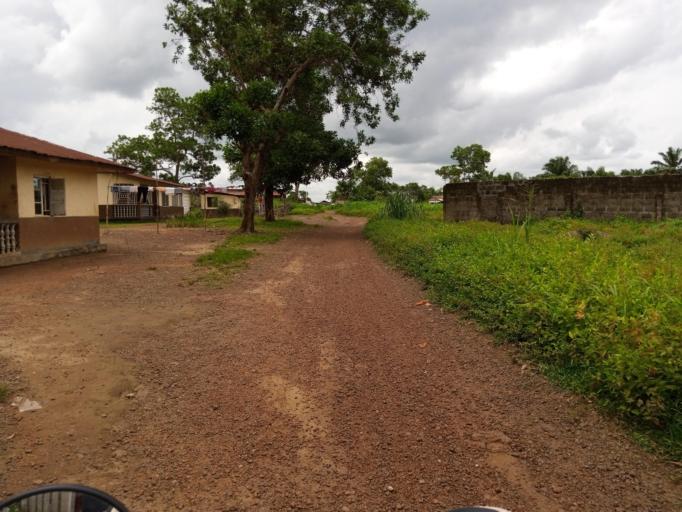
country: SL
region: Southern Province
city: Moyamba
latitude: 8.1640
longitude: -12.4245
